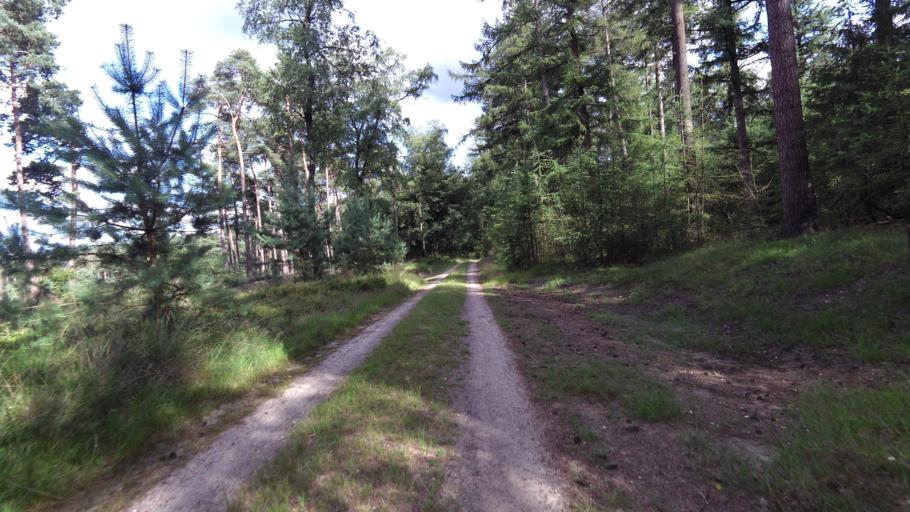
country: NL
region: Gelderland
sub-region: Gemeente Apeldoorn
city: Uddel
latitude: 52.2830
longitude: 5.8615
